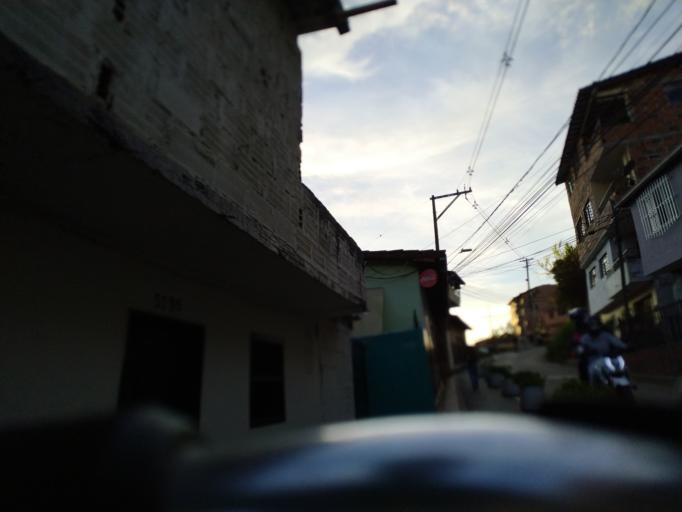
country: CO
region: Antioquia
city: Rionegro
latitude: 6.1583
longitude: -75.3761
